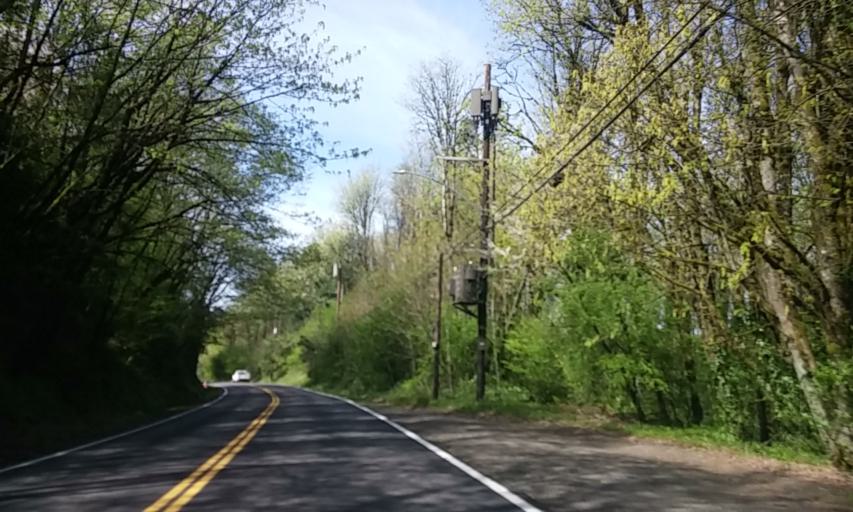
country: US
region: Oregon
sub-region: Washington County
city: West Haven-Sylvan
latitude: 45.5185
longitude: -122.7408
